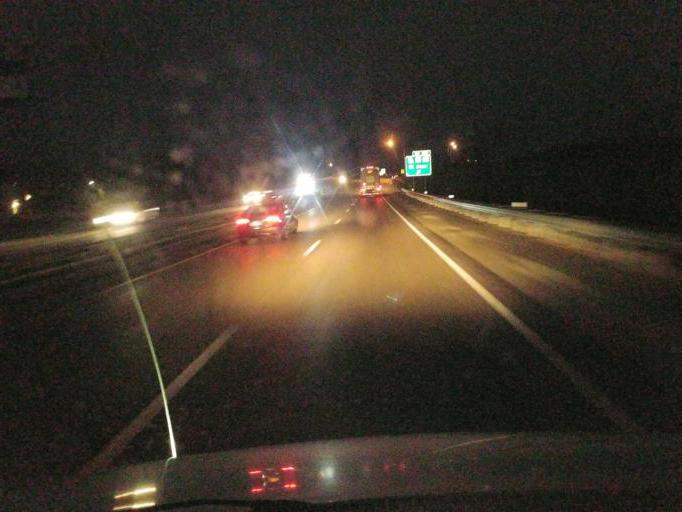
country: US
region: Missouri
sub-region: Franklin County
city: Saint Clair
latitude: 38.3477
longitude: -90.9906
